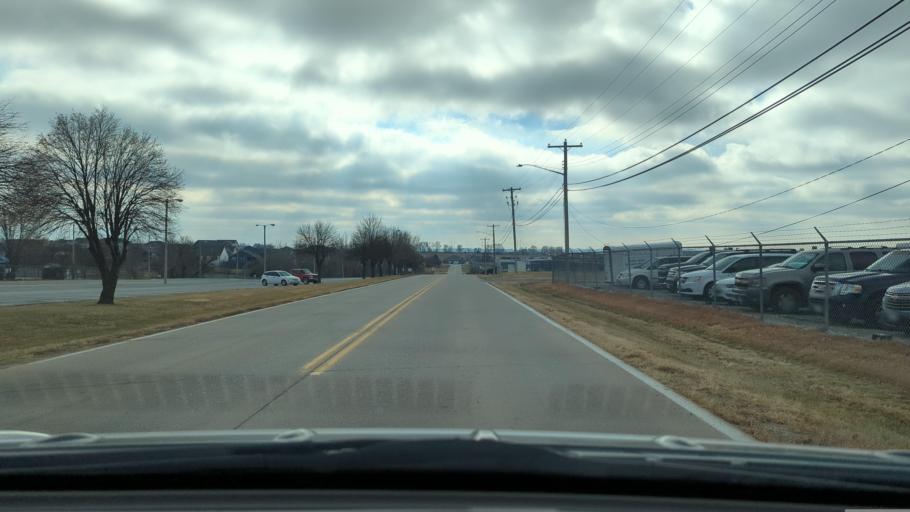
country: US
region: Nebraska
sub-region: Cass County
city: Plattsmouth
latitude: 41.0000
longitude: -95.9074
